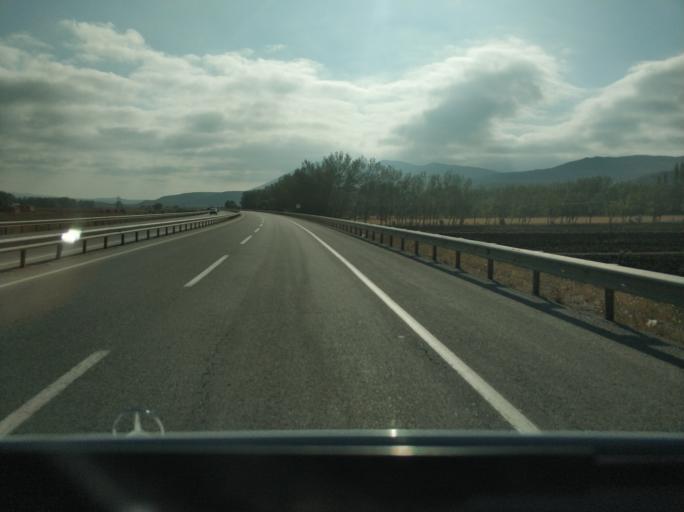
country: TR
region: Sivas
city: Yildizeli
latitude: 39.8481
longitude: 36.5221
